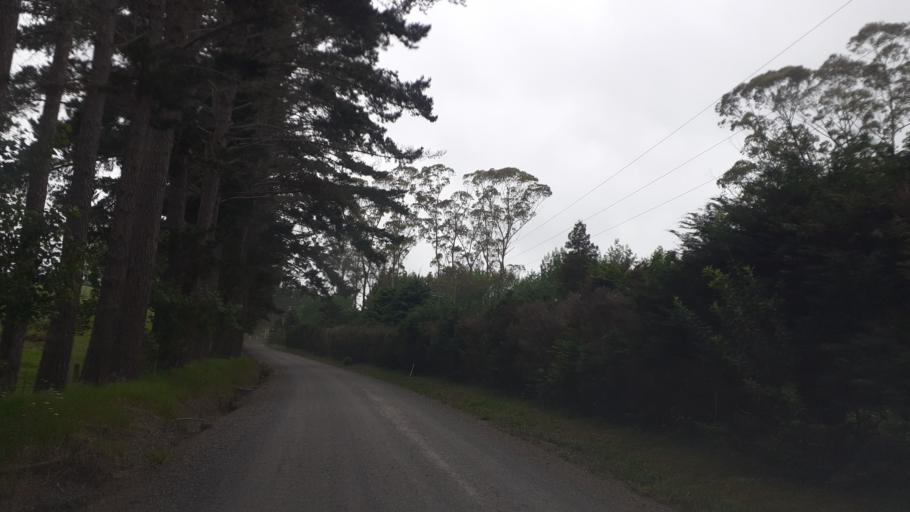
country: NZ
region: Northland
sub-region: Far North District
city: Kerikeri
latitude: -35.2816
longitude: 173.9591
